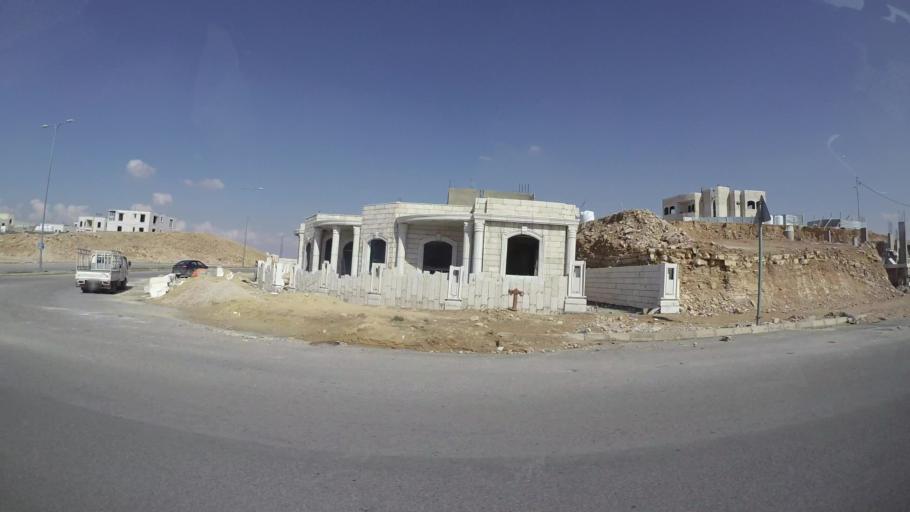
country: JO
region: Zarqa
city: Zarqa
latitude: 32.0488
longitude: 36.1160
